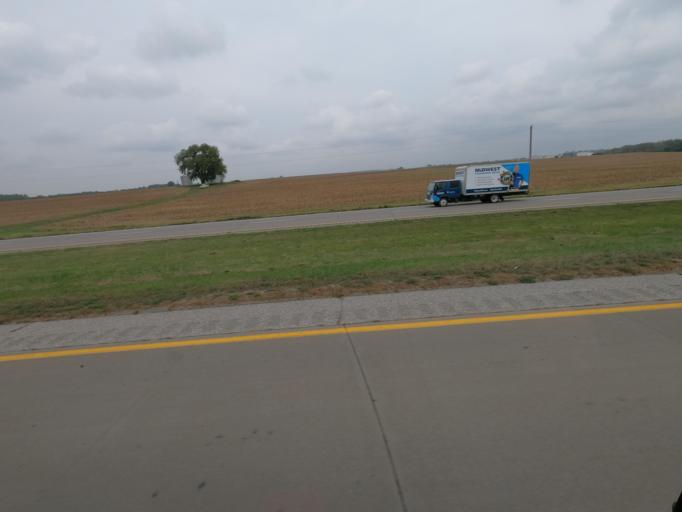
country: US
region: Iowa
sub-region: Wapello County
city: Eddyville
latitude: 41.1393
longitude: -92.5983
